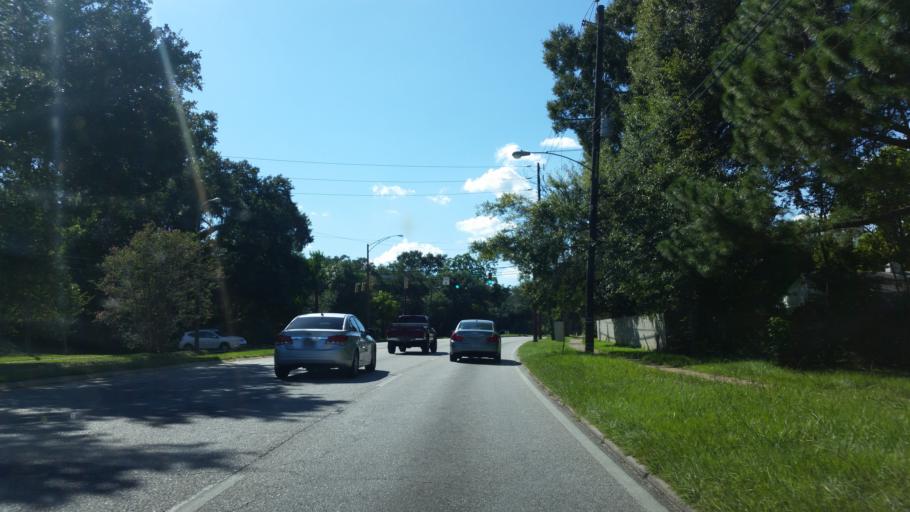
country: US
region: Alabama
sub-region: Mobile County
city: Mobile
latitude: 30.6916
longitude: -88.0906
